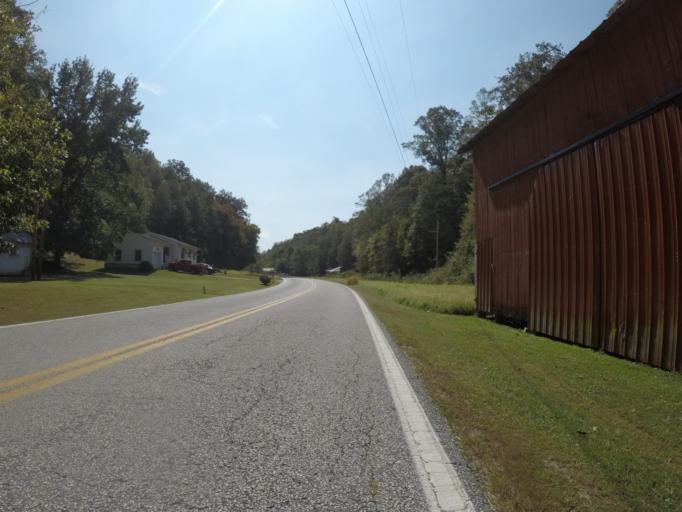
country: US
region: West Virginia
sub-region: Cabell County
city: Lesage
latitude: 38.5706
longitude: -82.4024
